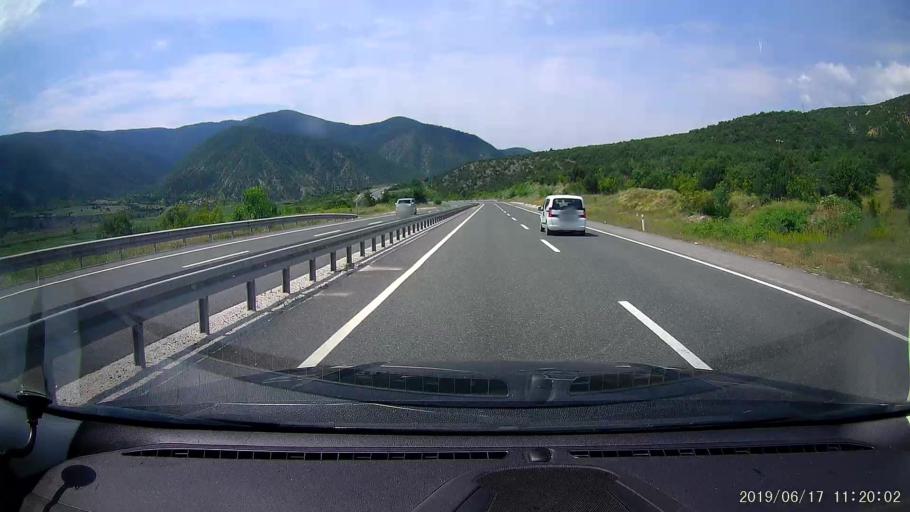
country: TR
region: Cankiri
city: Yaprakli
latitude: 40.9185
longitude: 33.8150
